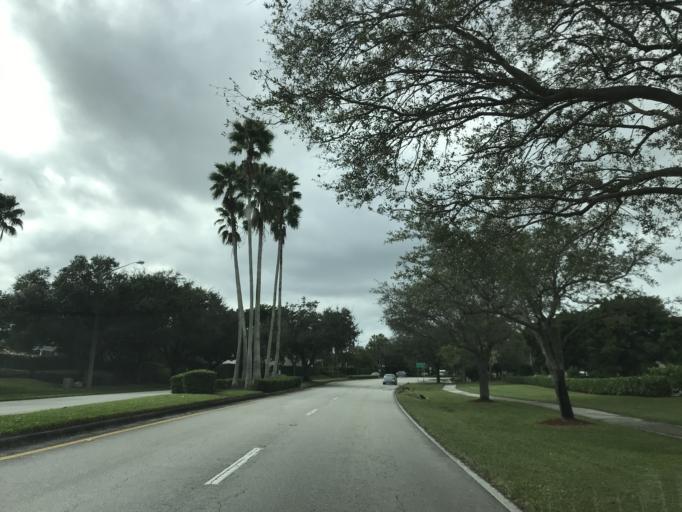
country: US
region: Florida
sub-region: Broward County
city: Coral Springs
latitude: 26.2979
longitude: -80.2754
